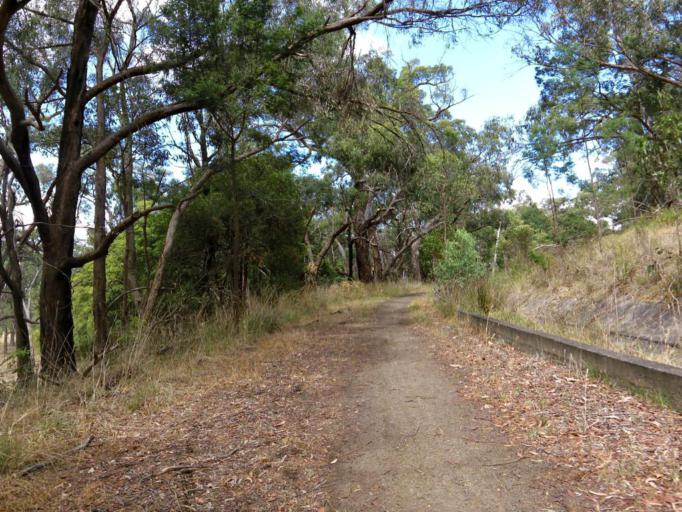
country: AU
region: Victoria
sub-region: Cardinia
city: Officer
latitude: -38.0388
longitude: 145.4578
